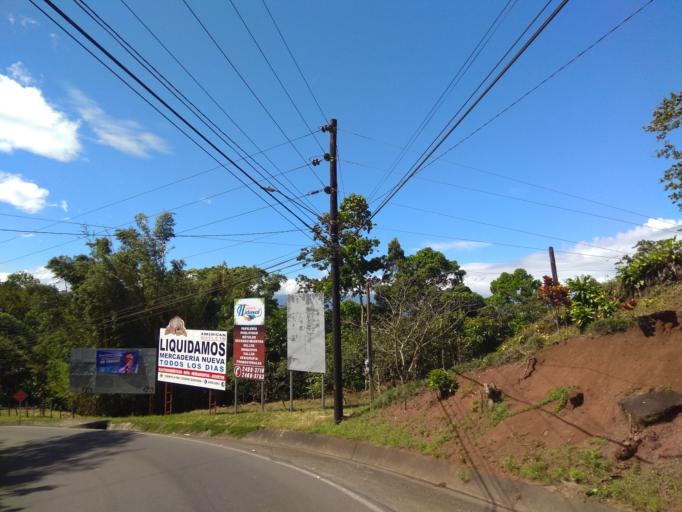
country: CR
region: Alajuela
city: Quesada
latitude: 10.3630
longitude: -84.4505
